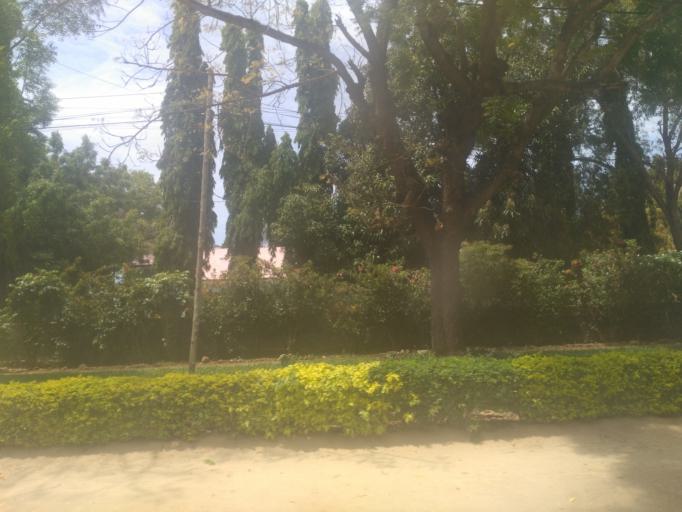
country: TZ
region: Zanzibar Urban/West
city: Zanzibar
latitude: -6.2110
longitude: 39.2109
